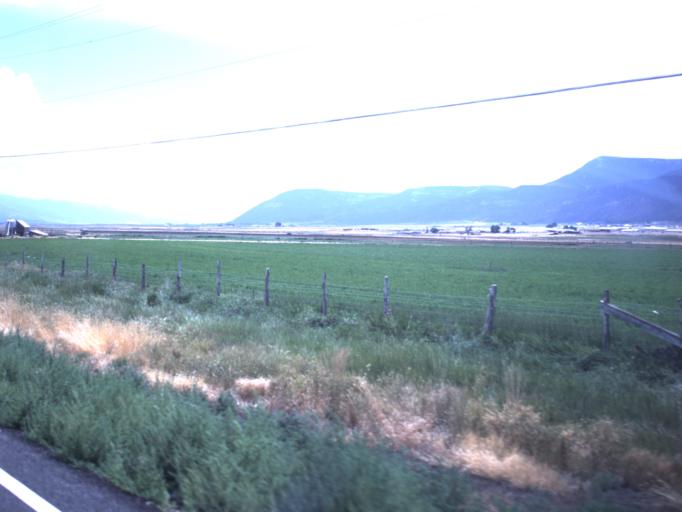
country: US
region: Utah
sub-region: Sanpete County
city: Fountain Green
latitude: 39.5830
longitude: -111.6132
